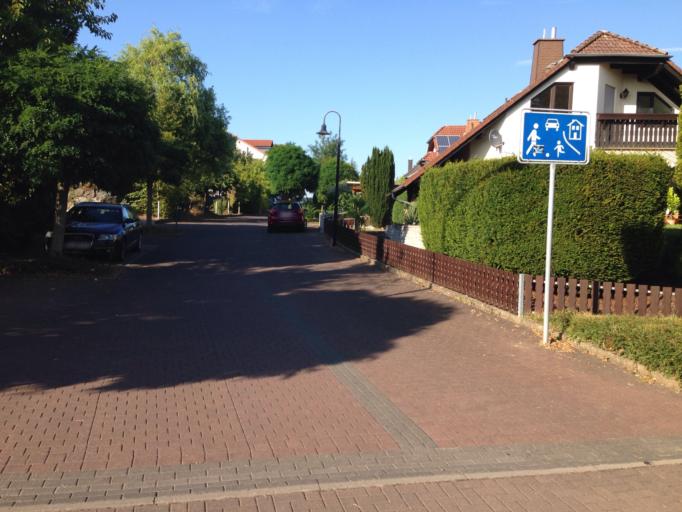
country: DE
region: Hesse
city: Lollar
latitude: 50.6389
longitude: 8.6723
